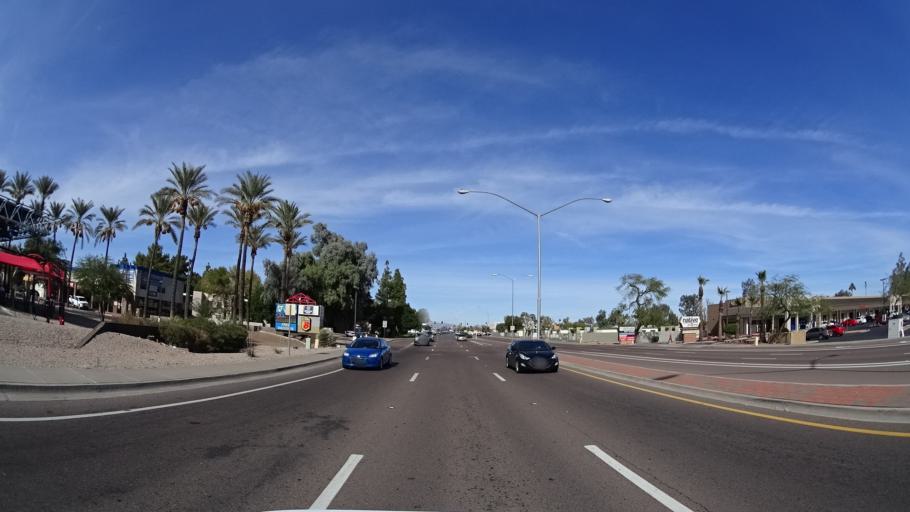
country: US
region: Arizona
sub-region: Maricopa County
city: Gilbert
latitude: 33.3880
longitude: -111.7884
